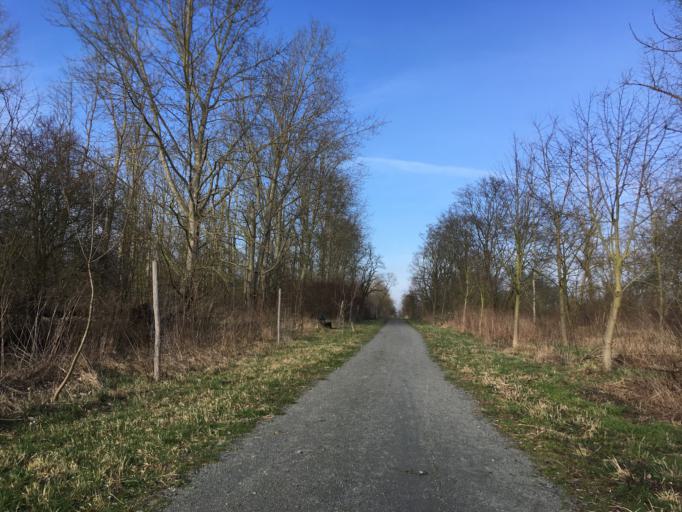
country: DE
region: Berlin
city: Blankenfelde
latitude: 52.6284
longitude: 13.4010
